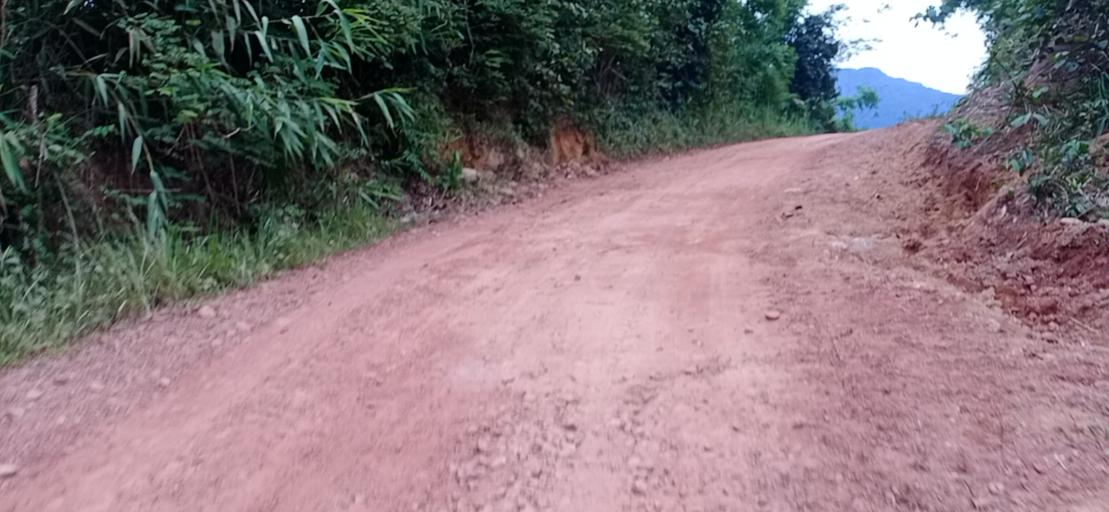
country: TH
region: Changwat Bueng Kan
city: Pak Khat
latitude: 18.5545
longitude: 103.1757
